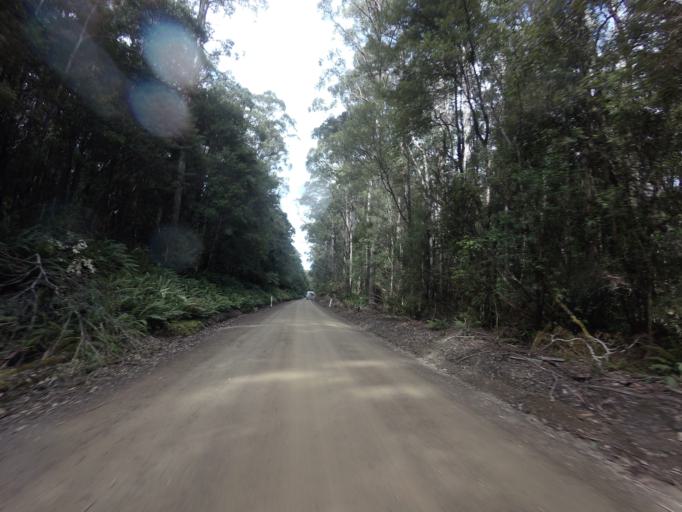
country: AU
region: Tasmania
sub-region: Huon Valley
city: Geeveston
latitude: -43.3928
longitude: 146.8550
